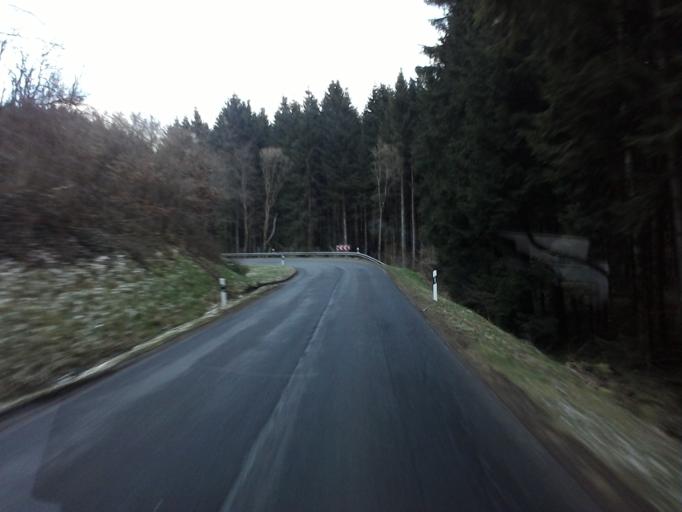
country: DE
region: Rheinland-Pfalz
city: Scheuern
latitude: 50.0306
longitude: 6.2996
